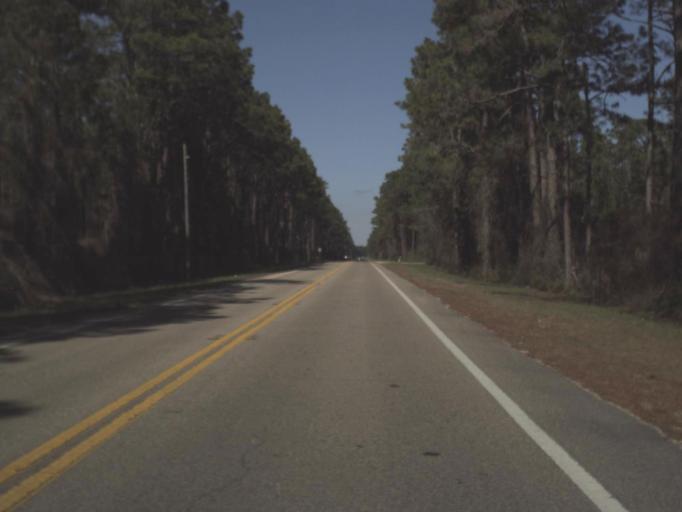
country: US
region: Florida
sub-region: Gulf County
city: Port Saint Joe
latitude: 29.8200
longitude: -85.2833
